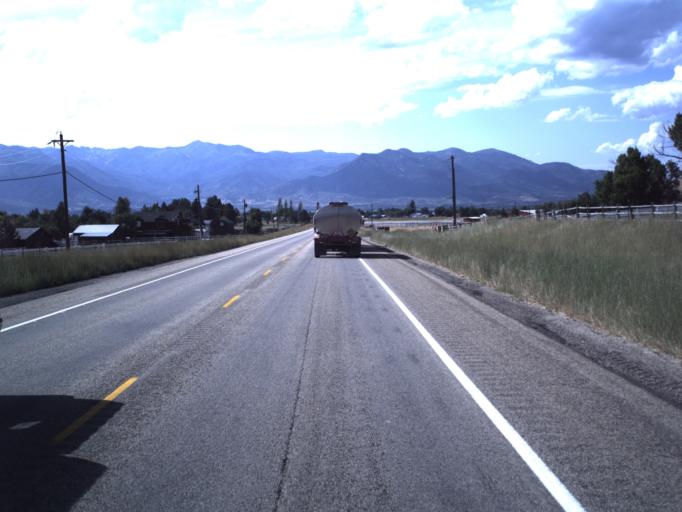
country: US
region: Utah
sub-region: Wasatch County
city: Heber
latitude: 40.4533
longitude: -111.3728
